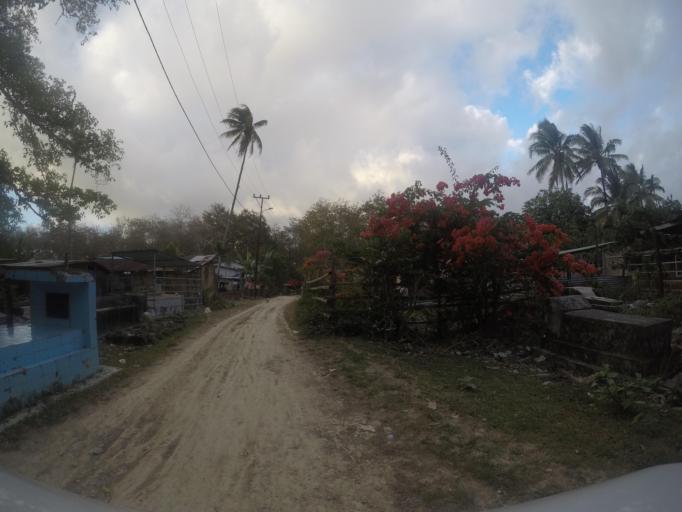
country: TL
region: Lautem
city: Lospalos
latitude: -8.5156
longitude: 126.9876
